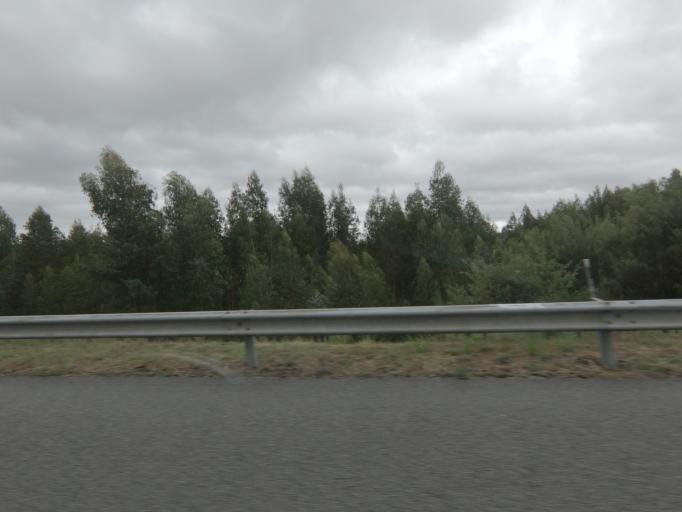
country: PT
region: Porto
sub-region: Paredes
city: Baltar
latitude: 41.1758
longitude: -8.3782
